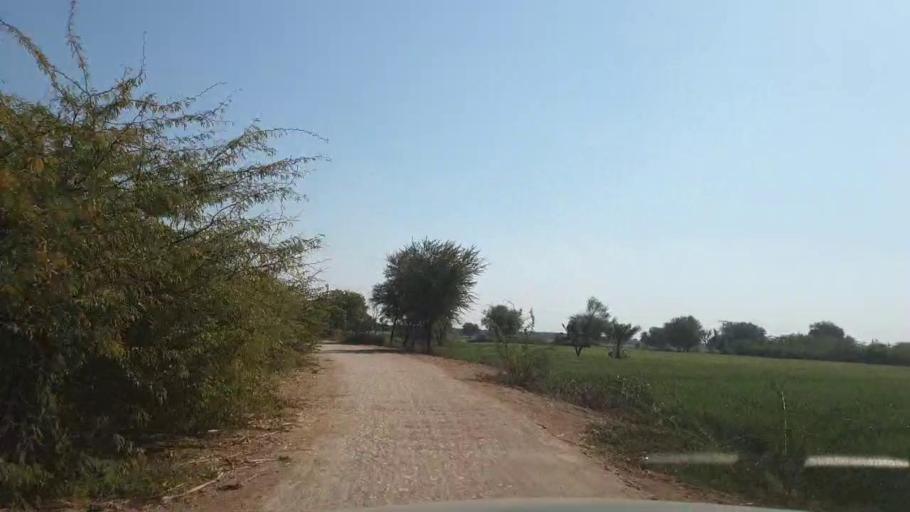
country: PK
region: Sindh
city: Tando Adam
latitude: 25.6390
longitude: 68.7061
